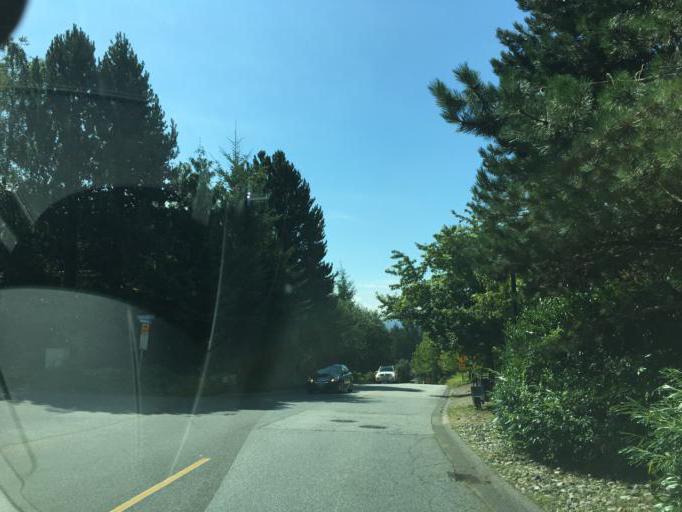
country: CA
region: British Columbia
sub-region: Greater Vancouver Regional District
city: Bowen Island
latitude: 49.3441
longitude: -123.2580
